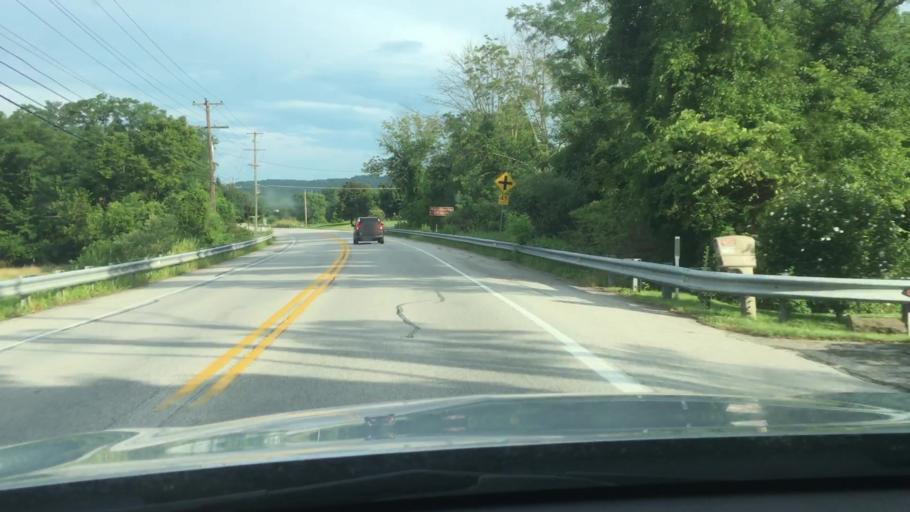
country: US
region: Pennsylvania
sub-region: York County
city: Dover
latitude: 40.0554
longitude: -76.9114
